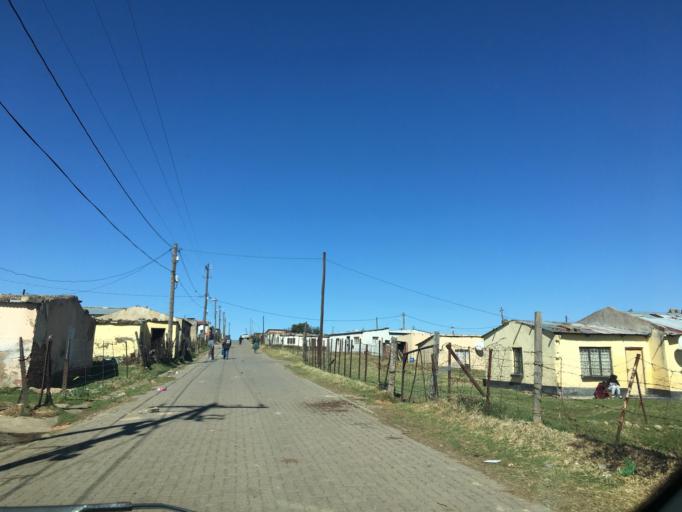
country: ZA
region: Eastern Cape
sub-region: Chris Hani District Municipality
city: Elliot
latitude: -31.3369
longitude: 27.8609
